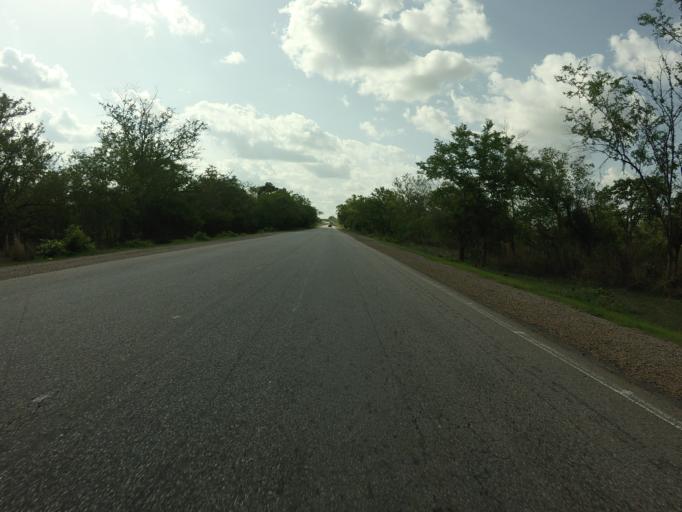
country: GH
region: Upper East
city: Bolgatanga
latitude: 10.5214
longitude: -0.8132
